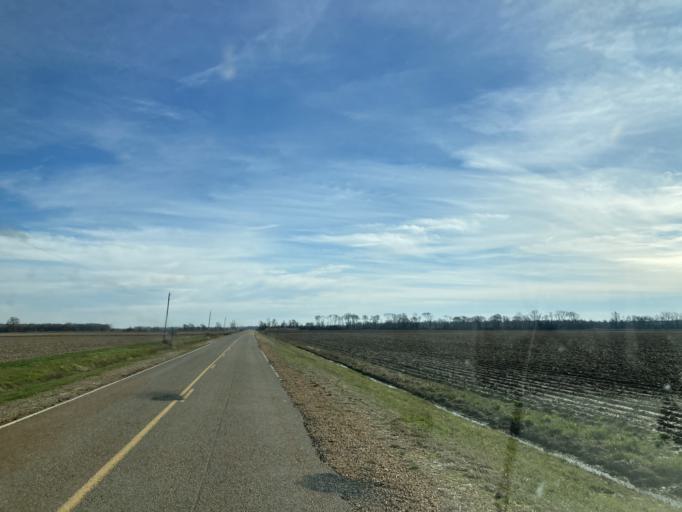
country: US
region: Mississippi
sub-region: Humphreys County
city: Belzoni
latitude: 33.0230
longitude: -90.6217
